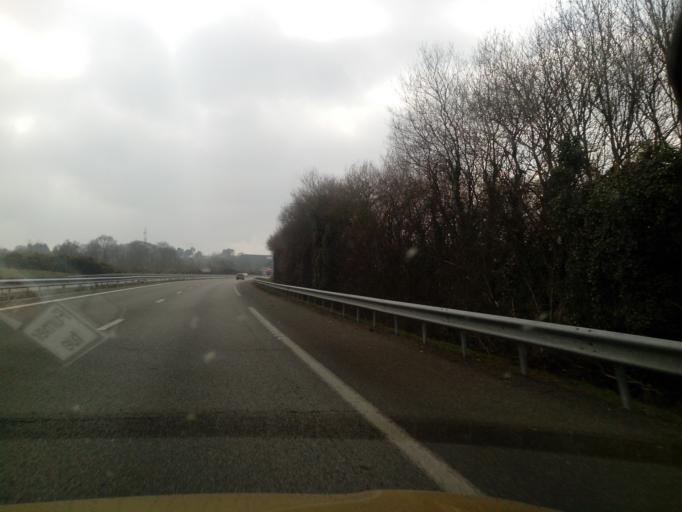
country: FR
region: Brittany
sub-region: Departement du Morbihan
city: Elven
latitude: 47.7294
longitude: -2.5834
